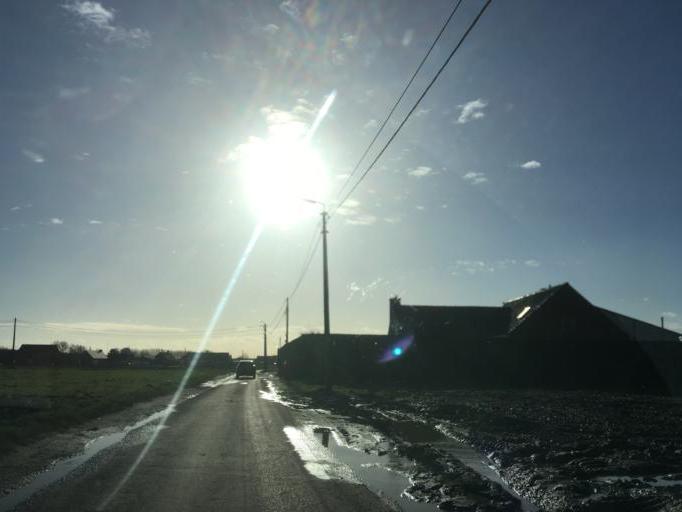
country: BE
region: Flanders
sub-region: Provincie West-Vlaanderen
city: Ardooie
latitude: 50.9821
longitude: 3.1735
